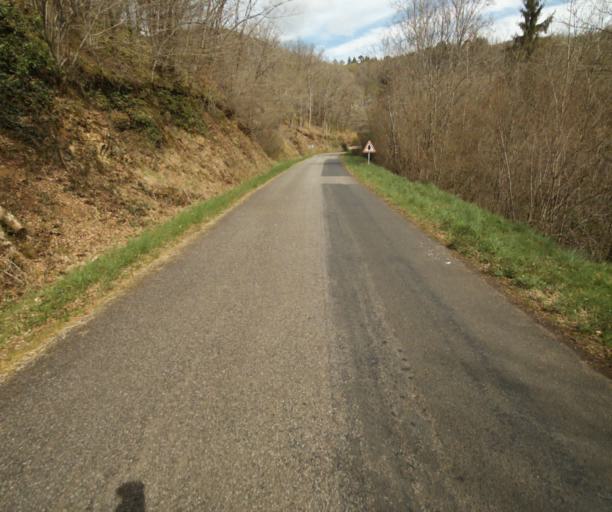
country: FR
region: Limousin
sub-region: Departement de la Correze
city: Laguenne
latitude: 45.2559
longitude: 1.8288
